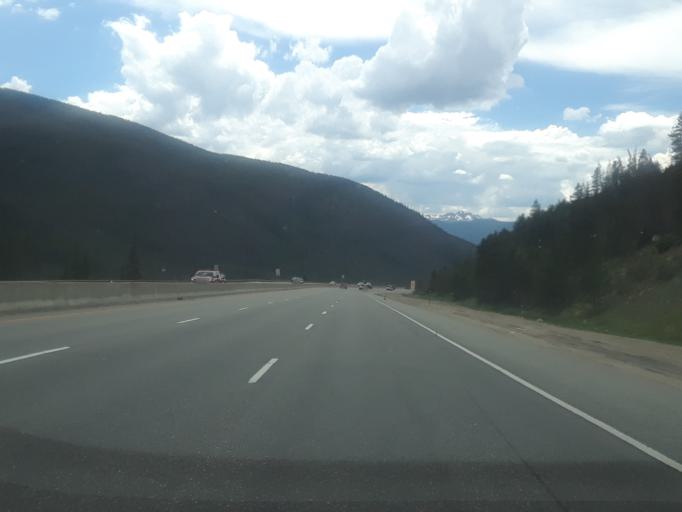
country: US
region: Colorado
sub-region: Summit County
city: Keystone
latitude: 39.6595
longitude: -105.9893
